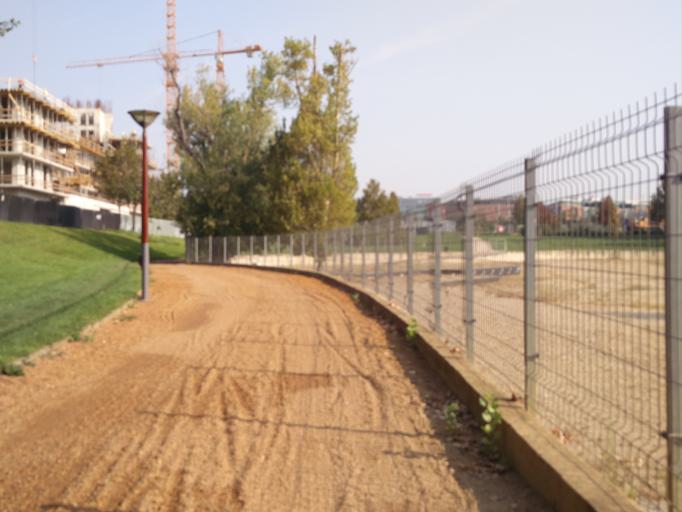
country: HU
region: Budapest
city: Budapest IX. keruelet
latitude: 47.4660
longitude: 19.0591
